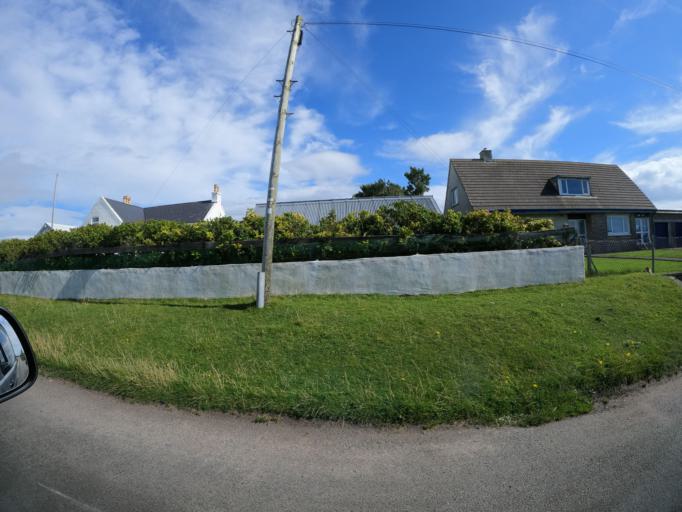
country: GB
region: Scotland
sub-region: Eilean Siar
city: Barra
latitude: 56.5036
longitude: -6.8075
